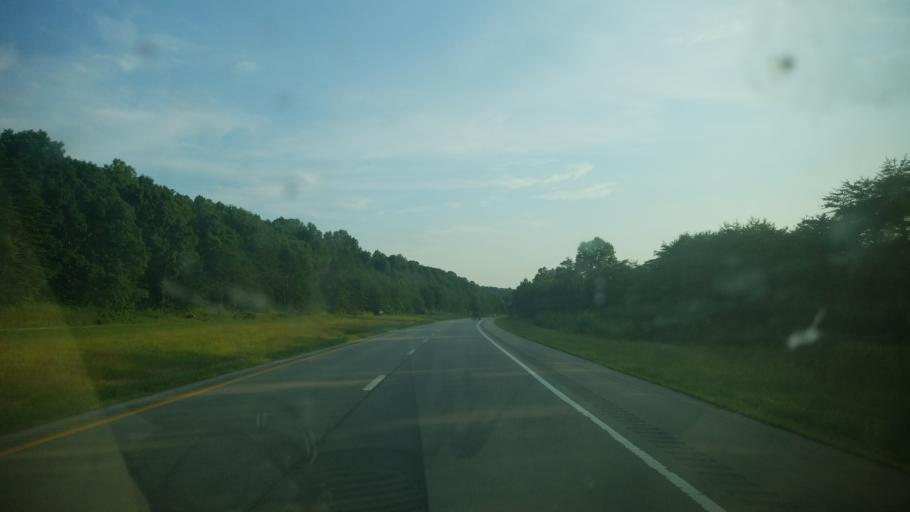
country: US
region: Ohio
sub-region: Adams County
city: Peebles
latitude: 38.9968
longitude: -83.3023
